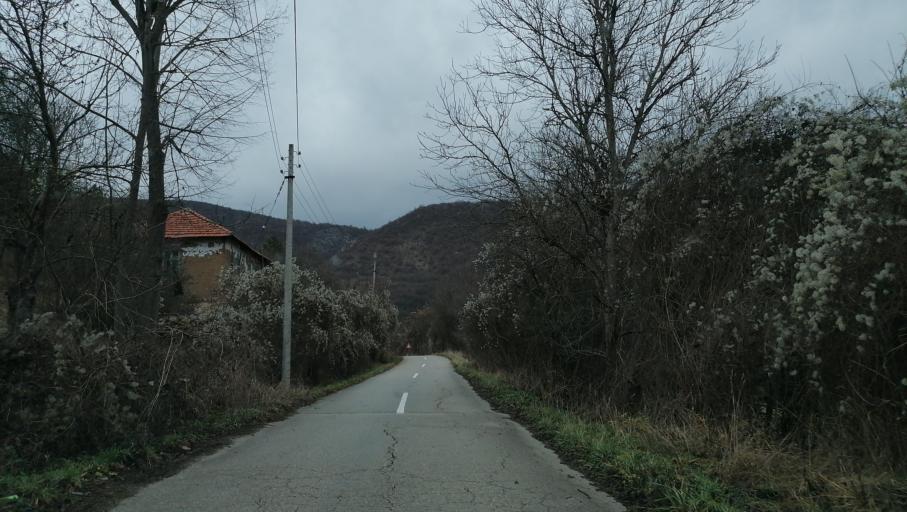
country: RS
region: Central Serbia
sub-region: Pirotski Okrug
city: Dimitrovgrad
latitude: 42.9311
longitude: 22.7735
